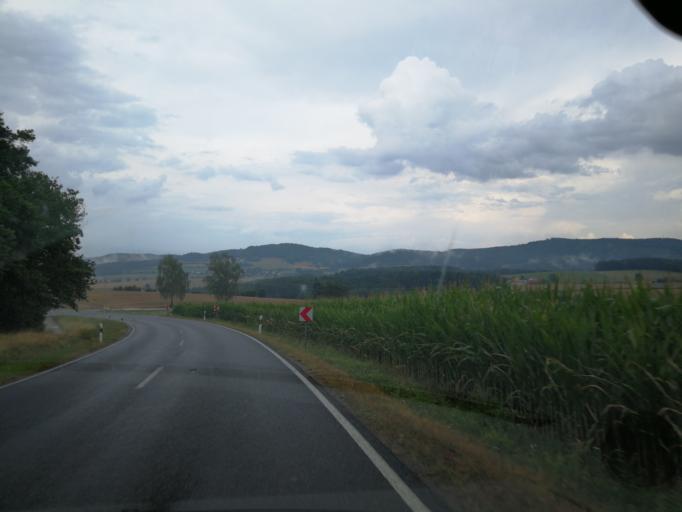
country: DE
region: Bavaria
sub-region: Upper Palatinate
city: Schorndorf
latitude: 49.1501
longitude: 12.5843
